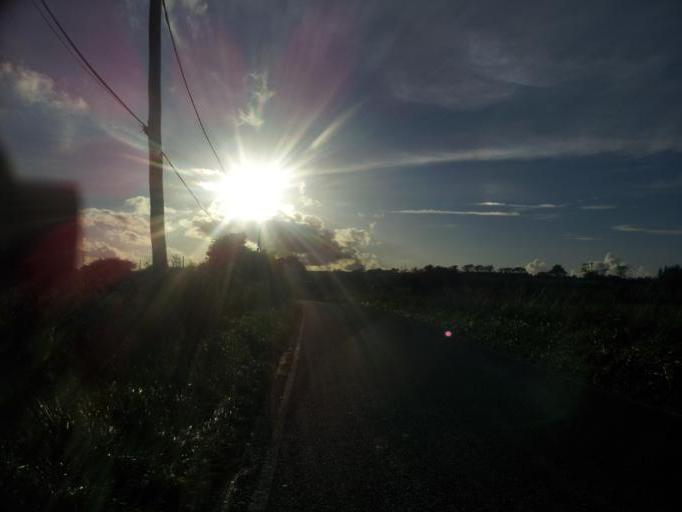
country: GB
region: England
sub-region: Kent
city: Newington
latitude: 51.3721
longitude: 0.6992
